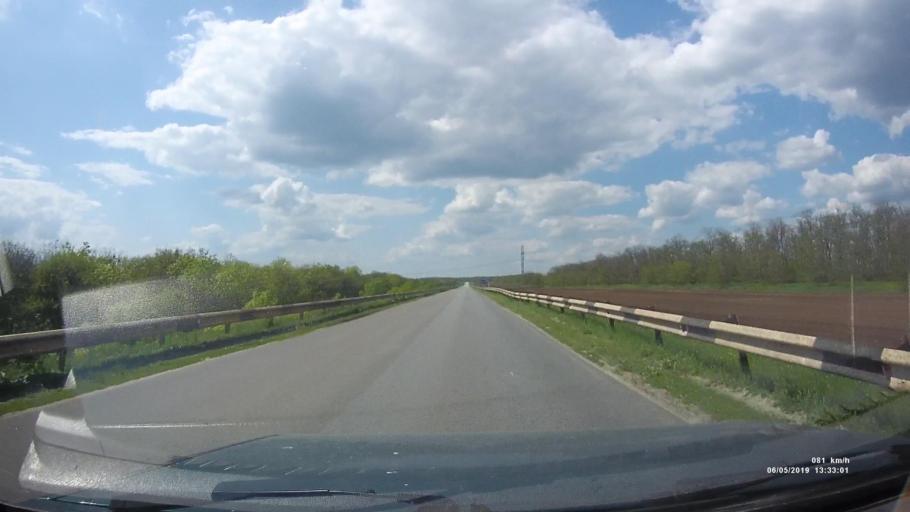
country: RU
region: Rostov
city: Ust'-Donetskiy
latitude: 47.6870
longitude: 40.7860
